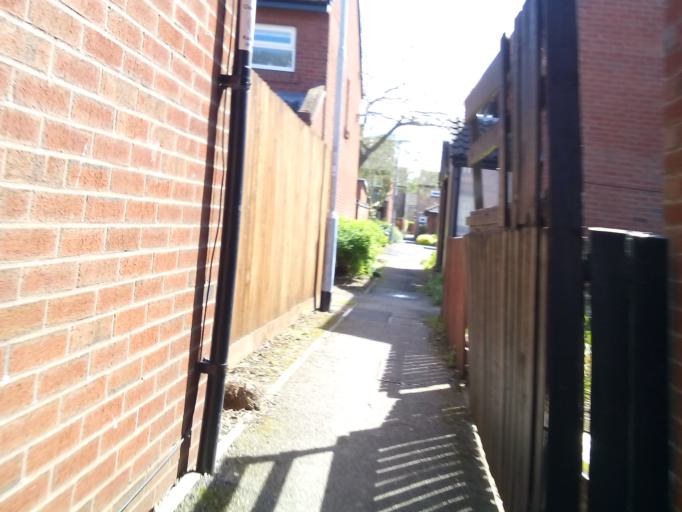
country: GB
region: England
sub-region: Cambridgeshire
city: Cambridge
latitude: 52.1940
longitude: 0.1579
